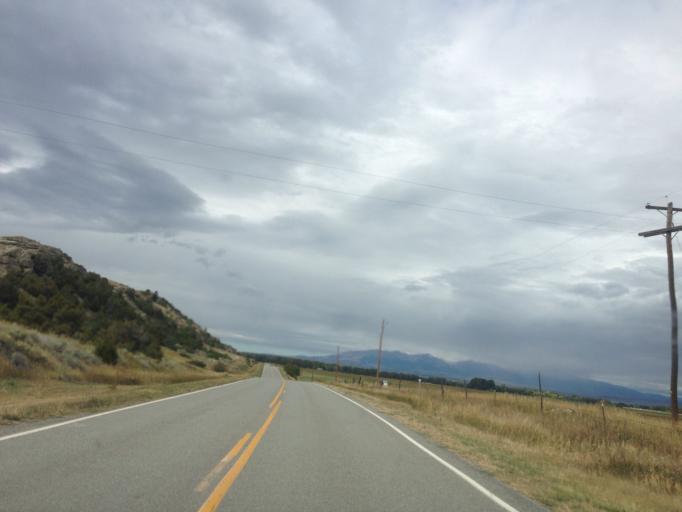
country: US
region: Montana
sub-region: Sweet Grass County
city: Big Timber
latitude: 45.7797
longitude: -109.8165
